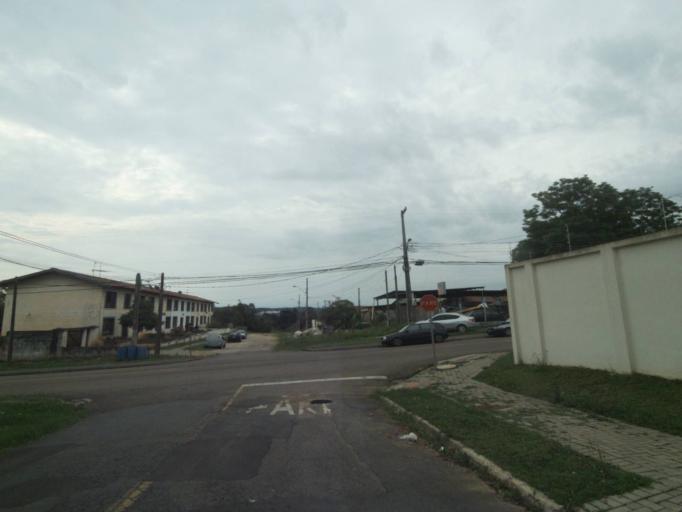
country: BR
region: Parana
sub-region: Curitiba
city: Curitiba
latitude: -25.3918
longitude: -49.2978
